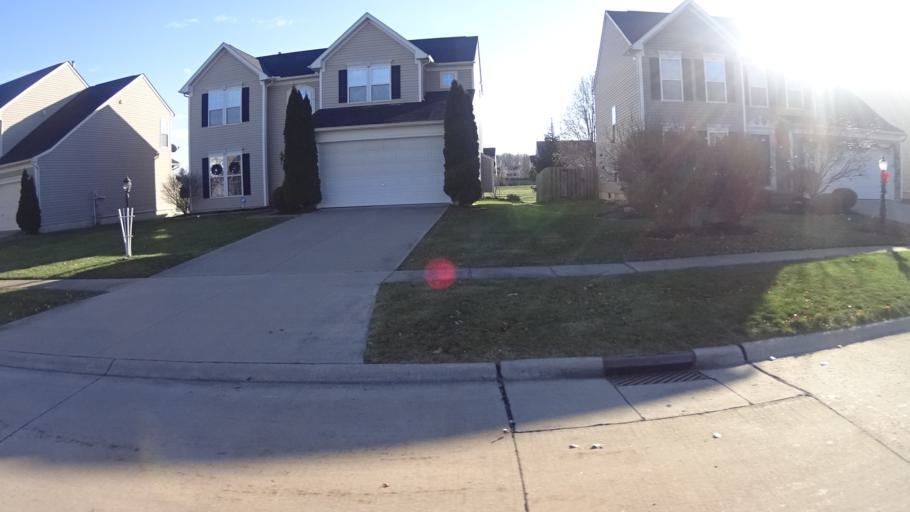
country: US
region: Ohio
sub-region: Lorain County
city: North Ridgeville
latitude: 41.4102
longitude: -82.0457
